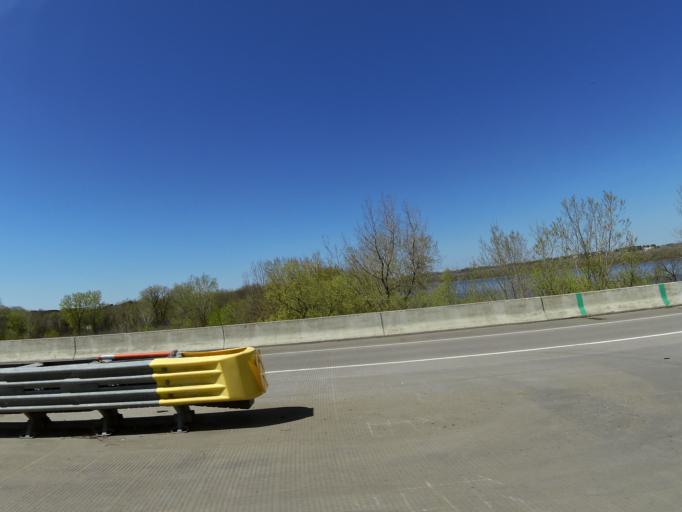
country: US
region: Minnesota
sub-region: Scott County
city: Savage
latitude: 44.7917
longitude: -93.4047
